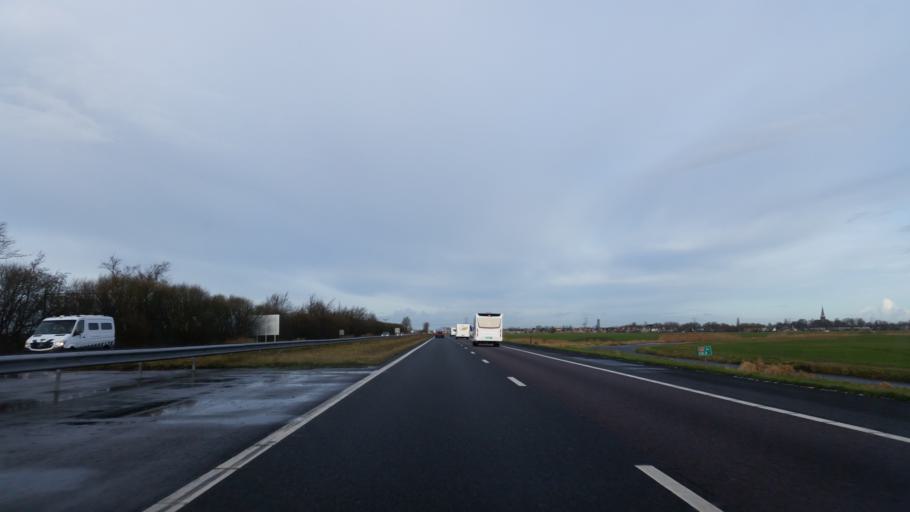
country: NL
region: Friesland
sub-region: Gemeente Leeuwarden
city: Wirdum
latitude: 53.1364
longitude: 5.8002
